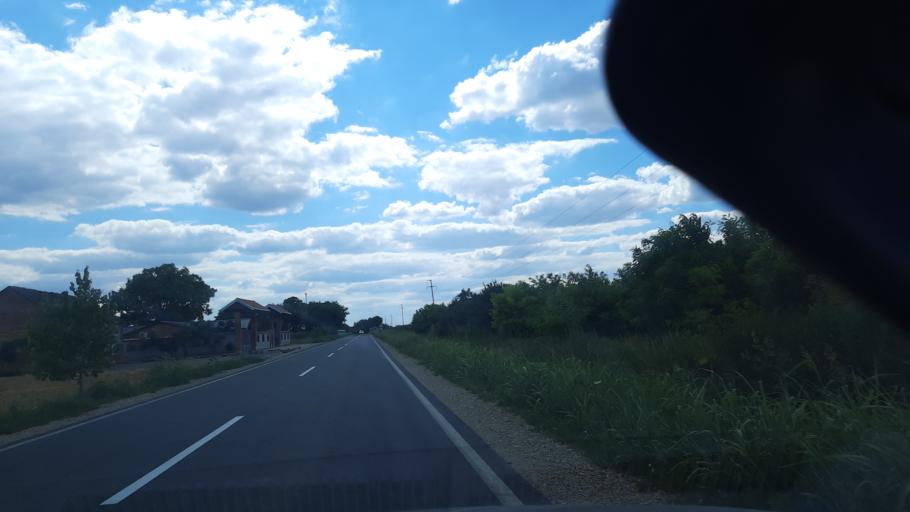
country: RS
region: Autonomna Pokrajina Vojvodina
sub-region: Sremski Okrug
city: Pecinci
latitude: 44.9205
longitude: 19.9780
